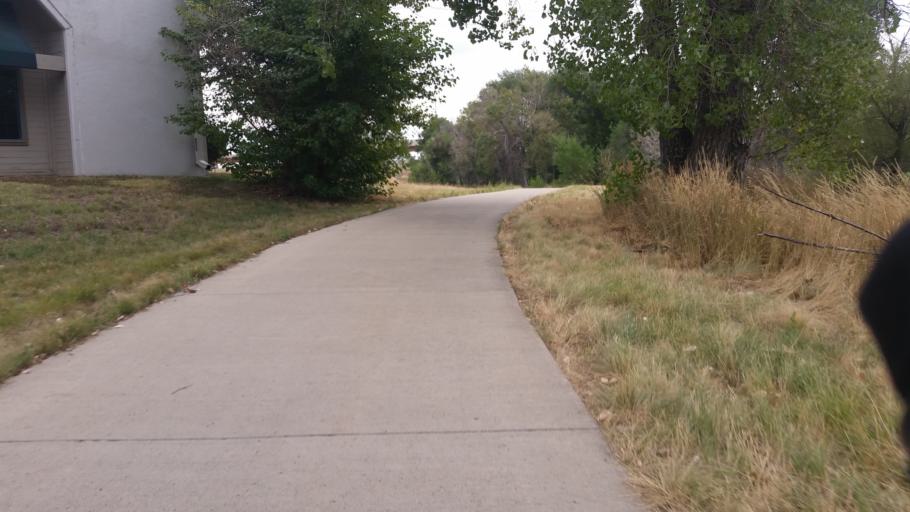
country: US
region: Colorado
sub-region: Adams County
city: Twin Lakes
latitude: 39.8193
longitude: -104.9866
